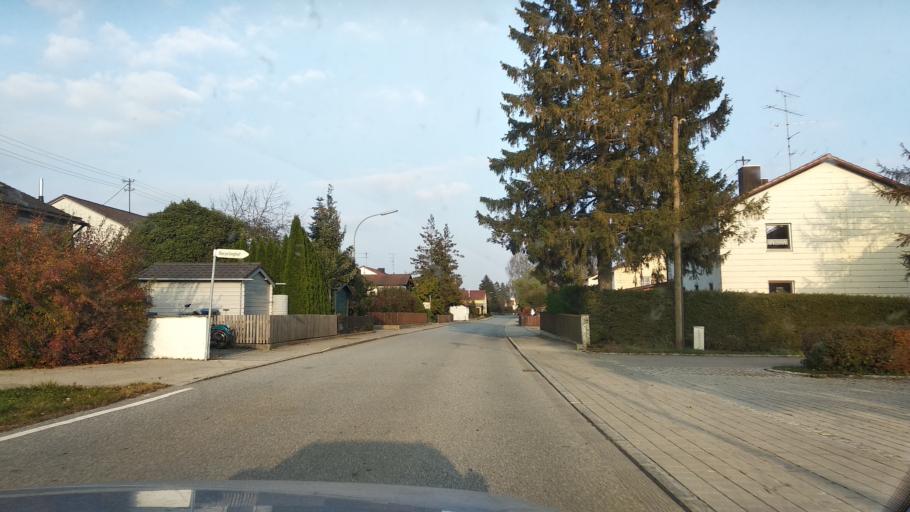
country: DE
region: Bavaria
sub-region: Upper Bavaria
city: Worth
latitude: 48.2424
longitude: 11.9301
